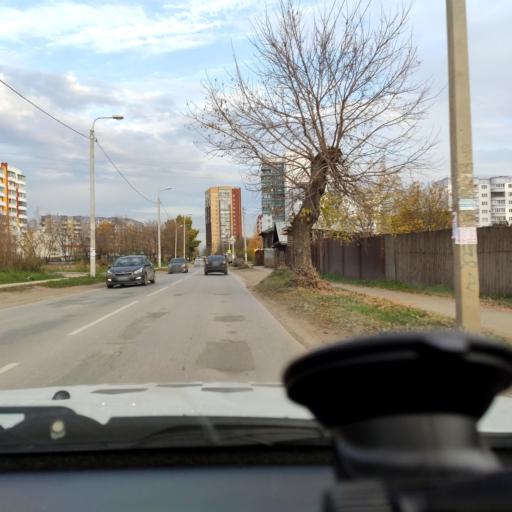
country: RU
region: Perm
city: Perm
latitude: 58.0309
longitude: 56.3273
